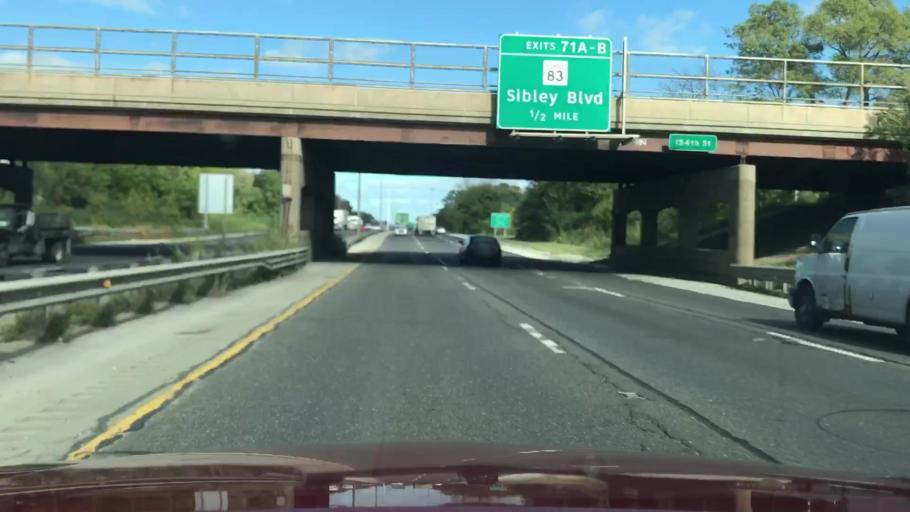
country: US
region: Illinois
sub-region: Cook County
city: South Holland
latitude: 41.6151
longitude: -87.5788
